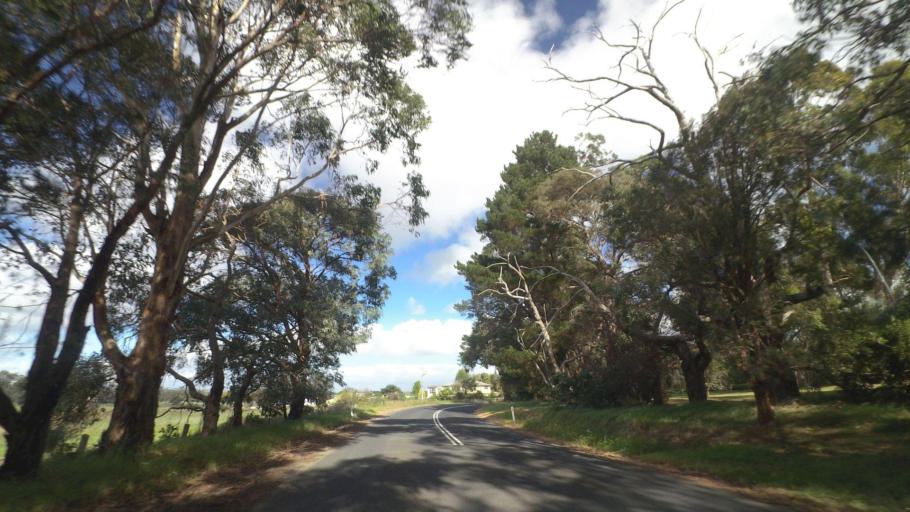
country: AU
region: Victoria
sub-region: Cardinia
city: Garfield
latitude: -38.0441
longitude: 145.6330
